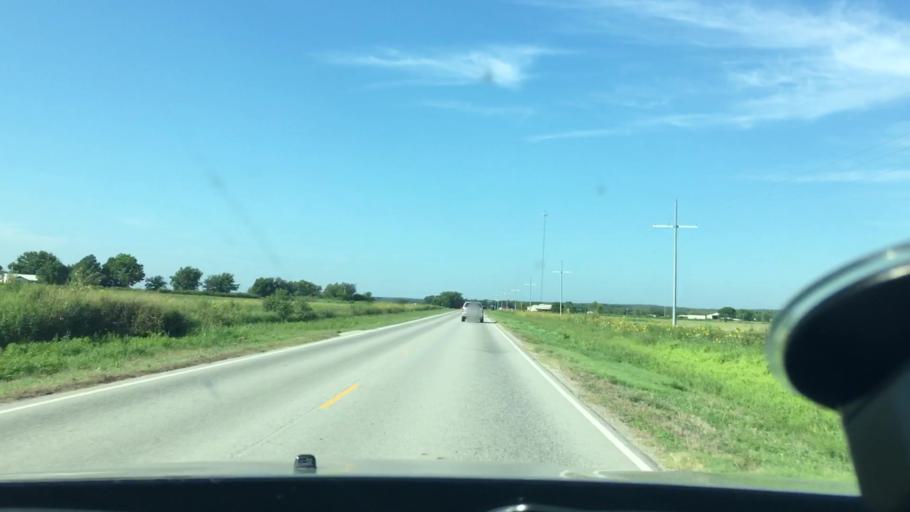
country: US
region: Oklahoma
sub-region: Coal County
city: Coalgate
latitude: 34.4945
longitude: -96.4158
